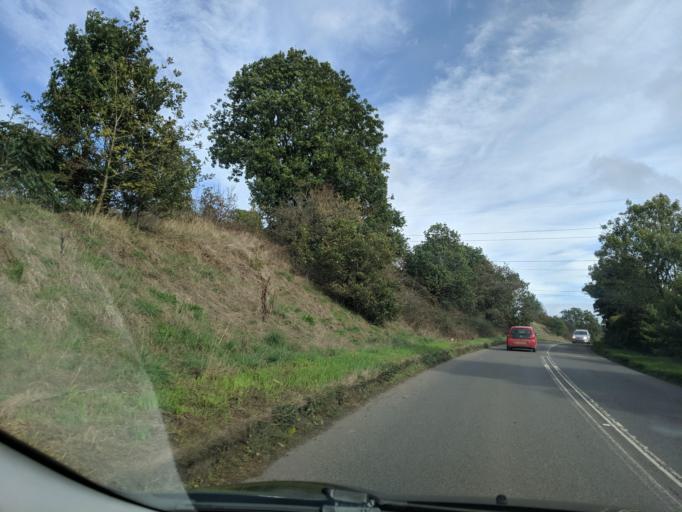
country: GB
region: England
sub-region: Devon
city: Ipplepen
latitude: 50.5357
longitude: -3.6702
